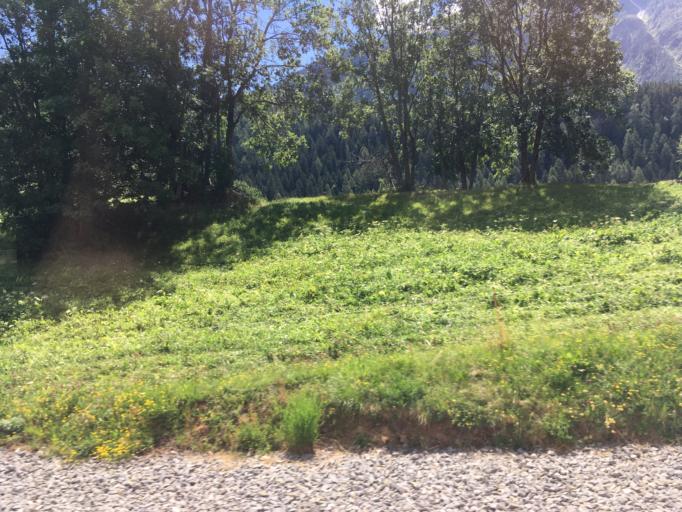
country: CH
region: Valais
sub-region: Goms District
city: Fiesch
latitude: 46.3863
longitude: 8.1163
